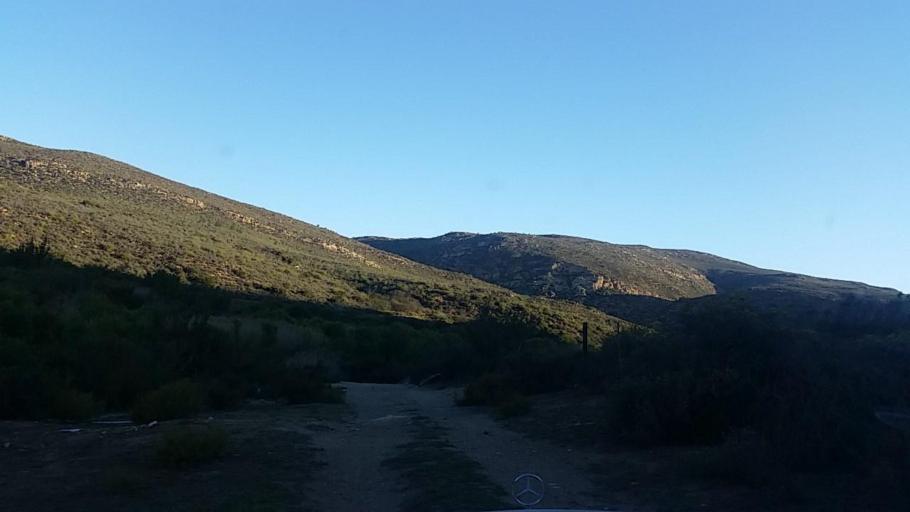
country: ZA
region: Western Cape
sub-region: Eden District Municipality
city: Knysna
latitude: -33.6609
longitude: 23.1383
